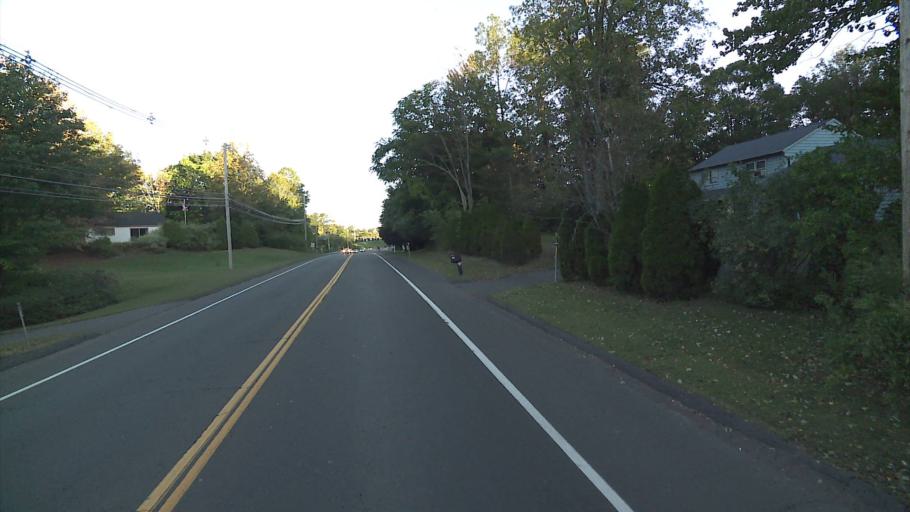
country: US
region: Connecticut
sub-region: New Haven County
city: Wallingford Center
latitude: 41.4753
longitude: -72.7637
